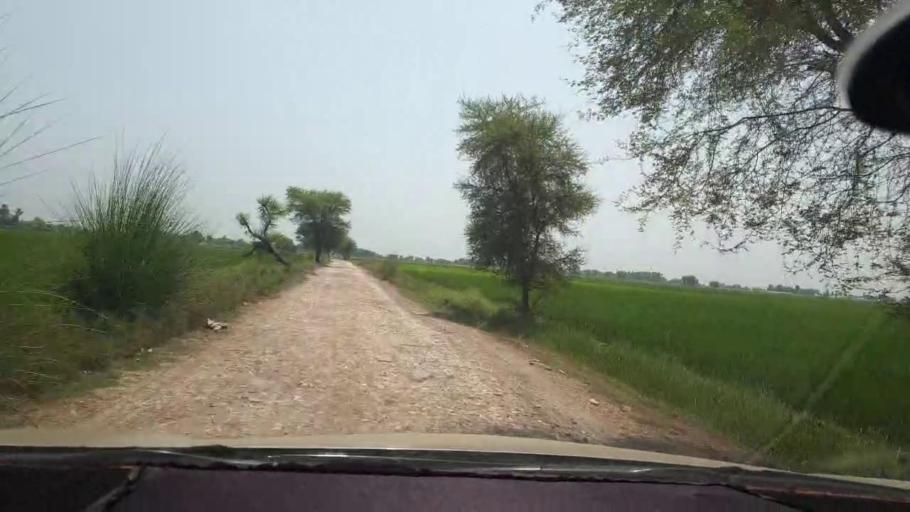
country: PK
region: Sindh
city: Kambar
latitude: 27.6454
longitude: 67.9319
